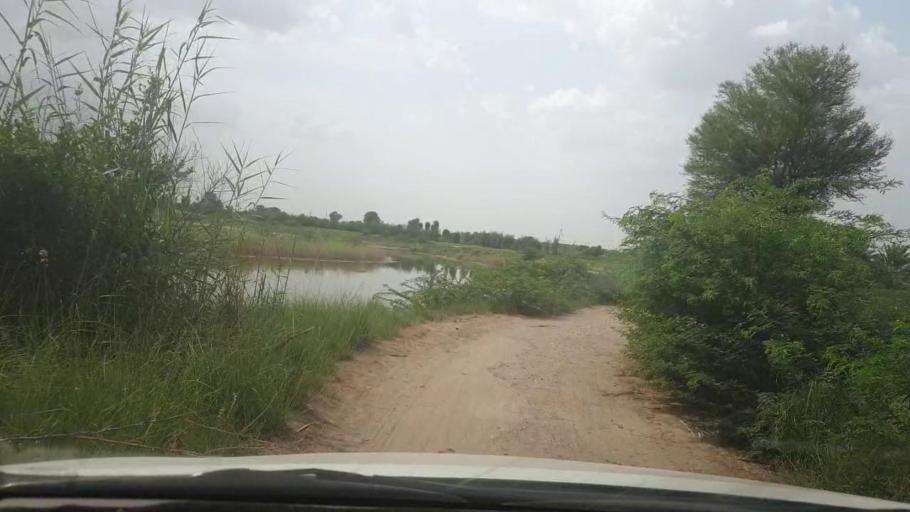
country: PK
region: Sindh
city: Kot Diji
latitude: 27.3347
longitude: 69.0078
